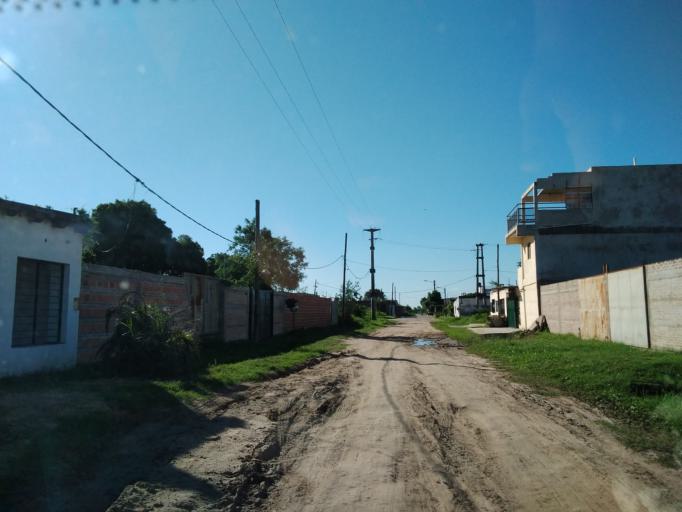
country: AR
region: Corrientes
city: Corrientes
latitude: -27.4596
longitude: -58.7699
